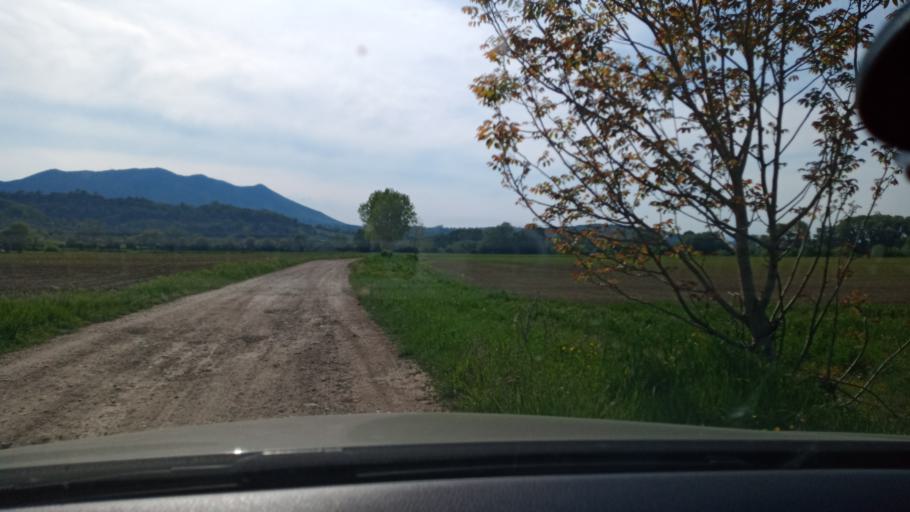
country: IT
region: Latium
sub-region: Citta metropolitana di Roma Capitale
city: Ponzano Romano
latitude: 42.2701
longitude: 12.5684
